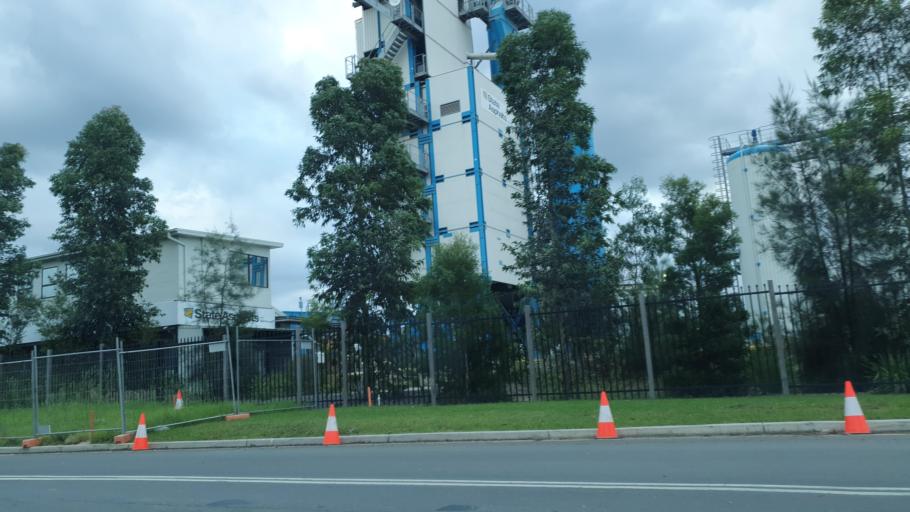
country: AU
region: New South Wales
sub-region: Penrith Municipality
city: Werrington County
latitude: -33.7374
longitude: 150.7676
